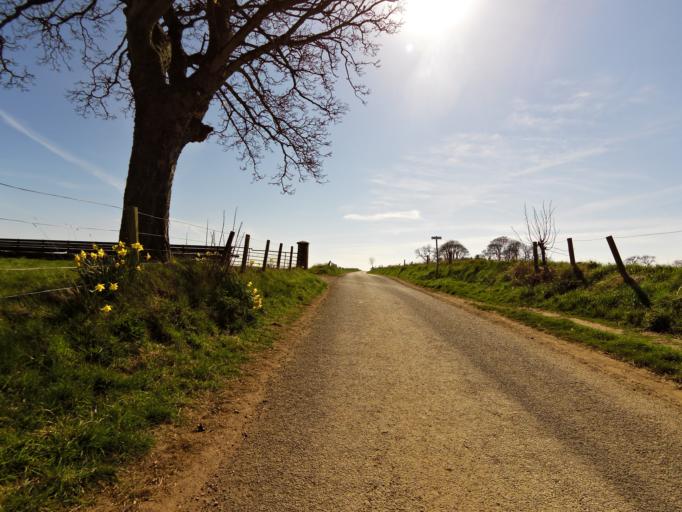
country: GB
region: Scotland
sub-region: Angus
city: Montrose
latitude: 56.6985
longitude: -2.4631
